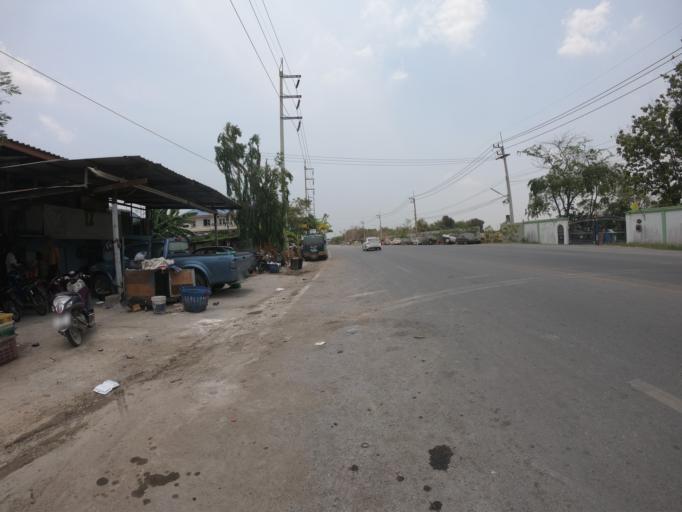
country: TH
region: Phra Nakhon Si Ayutthaya
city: Ban Bang Kadi Pathum Thani
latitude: 14.0104
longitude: 100.5715
